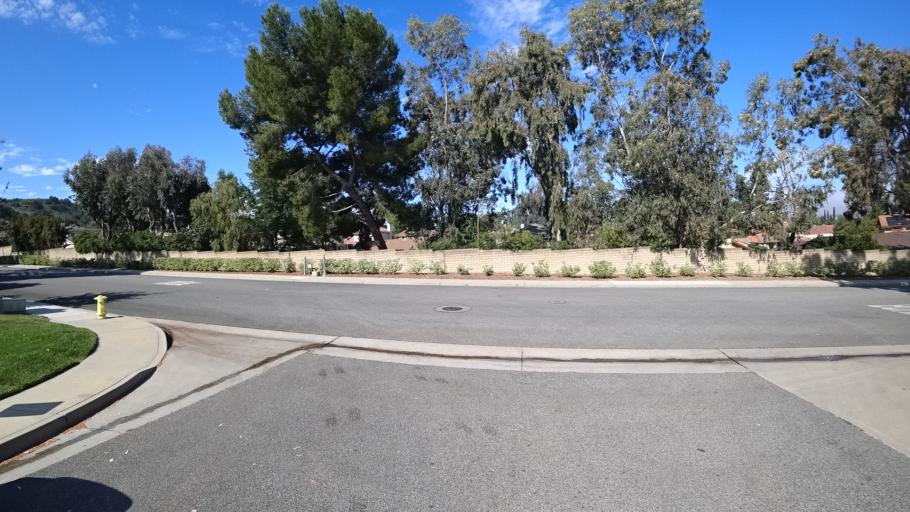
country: US
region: California
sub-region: Ventura County
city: Casa Conejo
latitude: 34.1795
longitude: -118.9291
